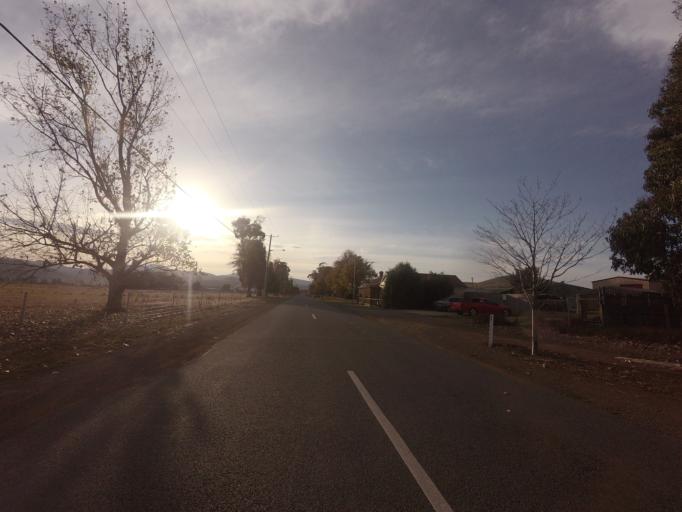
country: AU
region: Tasmania
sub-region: Brighton
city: Bridgewater
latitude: -42.5245
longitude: 147.1954
